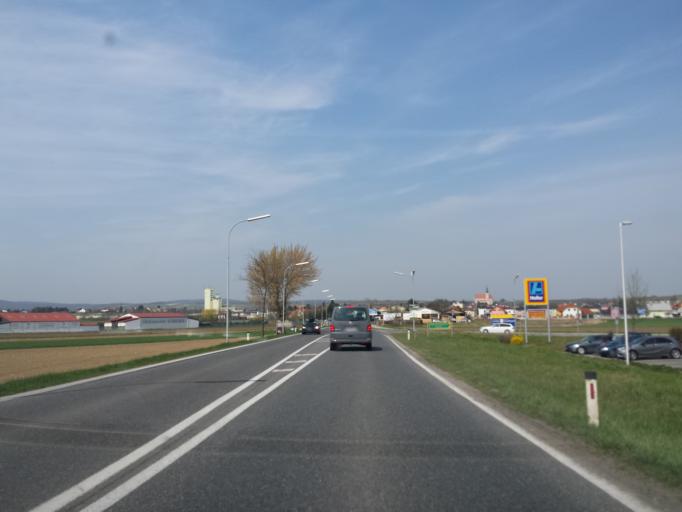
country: AT
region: Lower Austria
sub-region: Politischer Bezirk Mistelbach
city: Poysdorf
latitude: 48.6558
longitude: 16.6307
